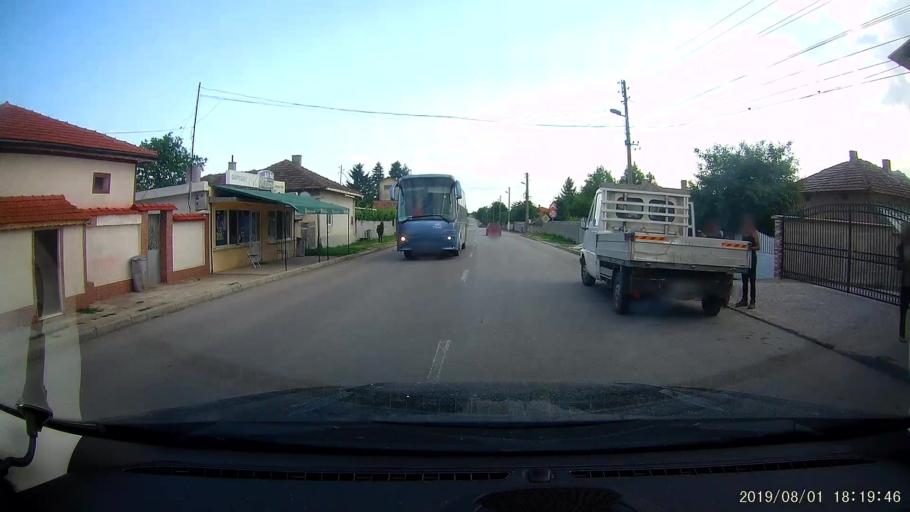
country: BG
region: Shumen
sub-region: Obshtina Kaolinovo
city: Kaolinovo
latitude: 43.6803
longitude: 27.0908
